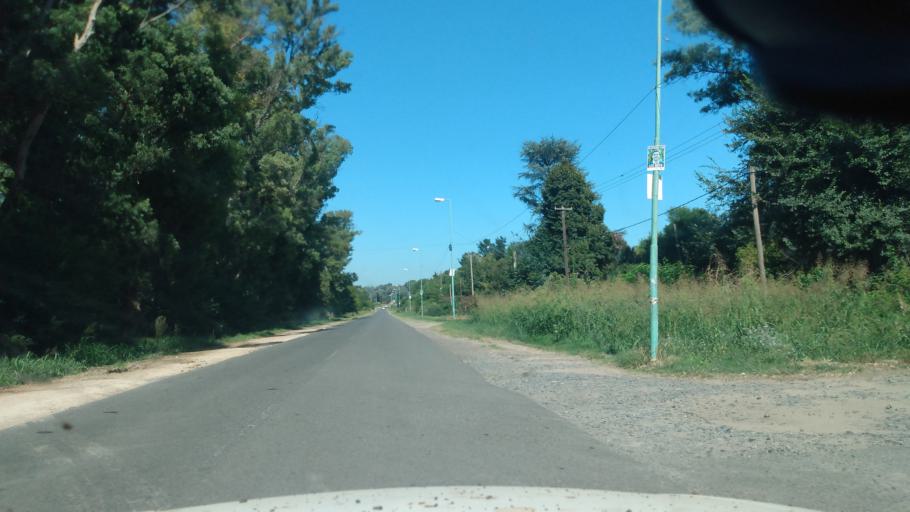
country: AR
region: Buenos Aires
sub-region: Partido de Lujan
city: Lujan
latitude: -34.5070
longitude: -59.0810
